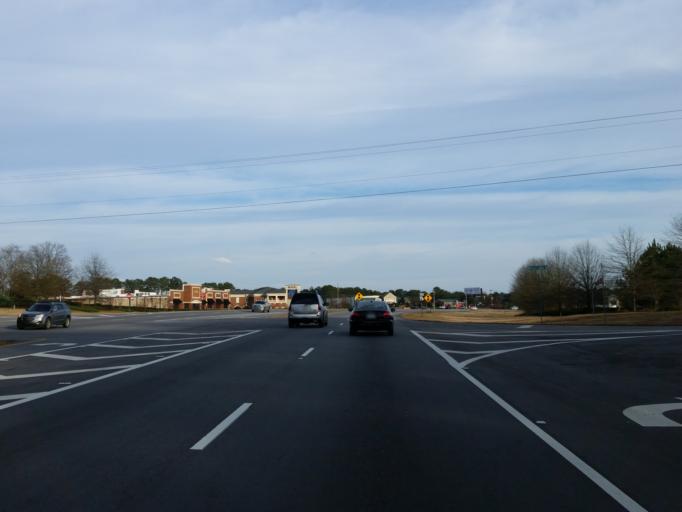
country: US
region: Georgia
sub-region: Paulding County
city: Hiram
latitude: 33.9024
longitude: -84.7755
